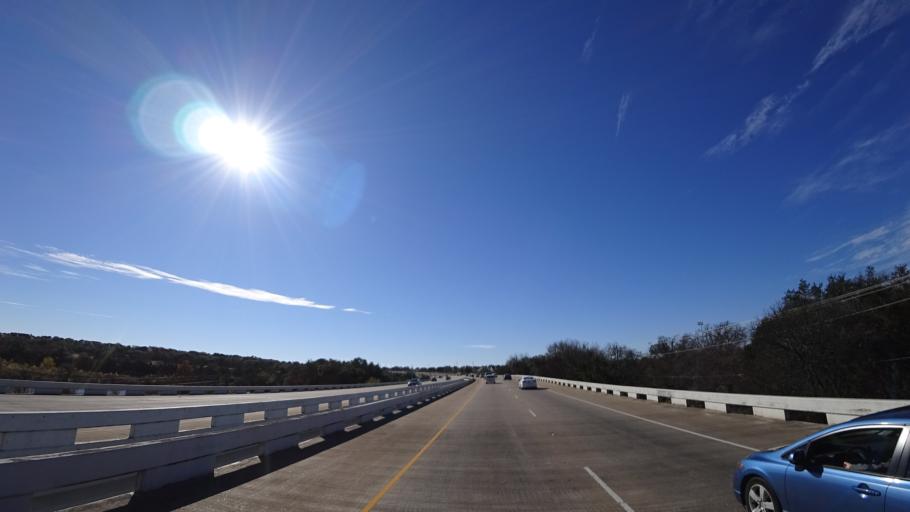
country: US
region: Texas
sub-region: Williamson County
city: Brushy Creek
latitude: 30.5065
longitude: -97.7761
